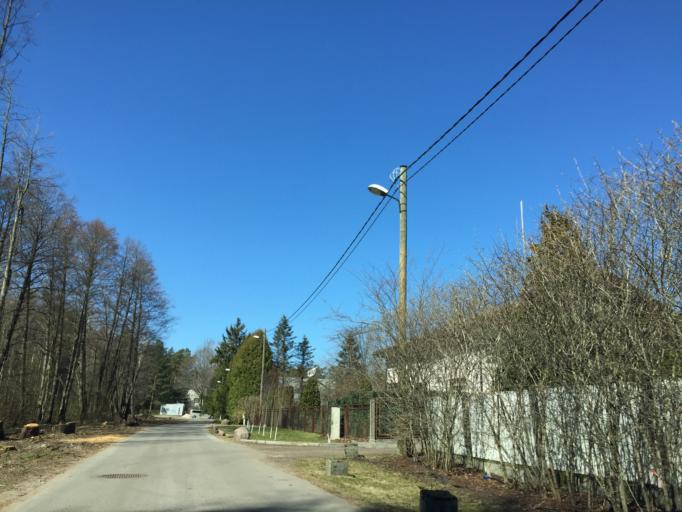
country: LV
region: Jurmala
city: Jurmala
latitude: 56.9406
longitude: 23.6877
